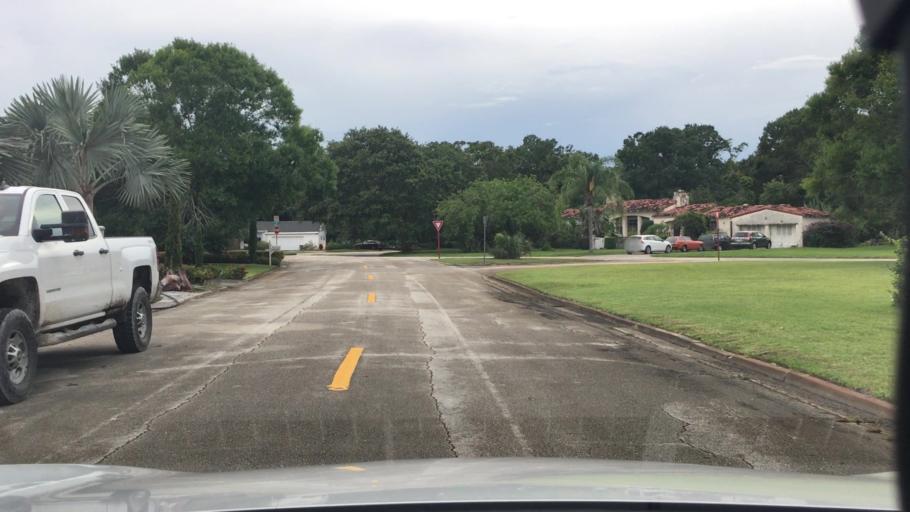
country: US
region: Florida
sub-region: Indian River County
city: Vero Beach
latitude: 27.6411
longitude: -80.4075
